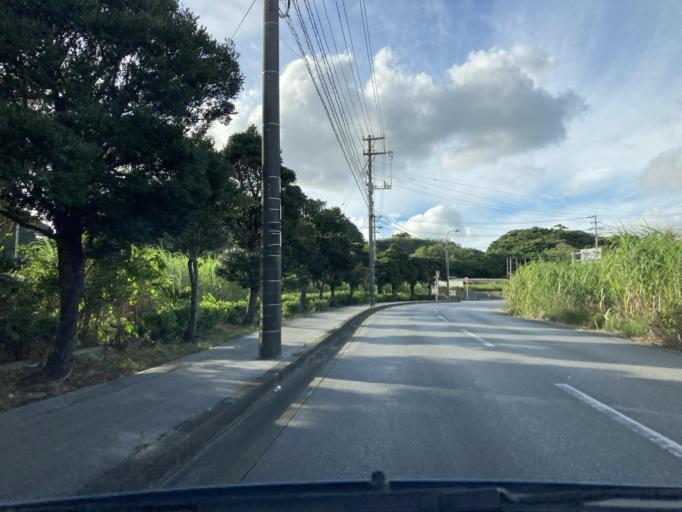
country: JP
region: Okinawa
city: Itoman
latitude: 26.1360
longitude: 127.7470
